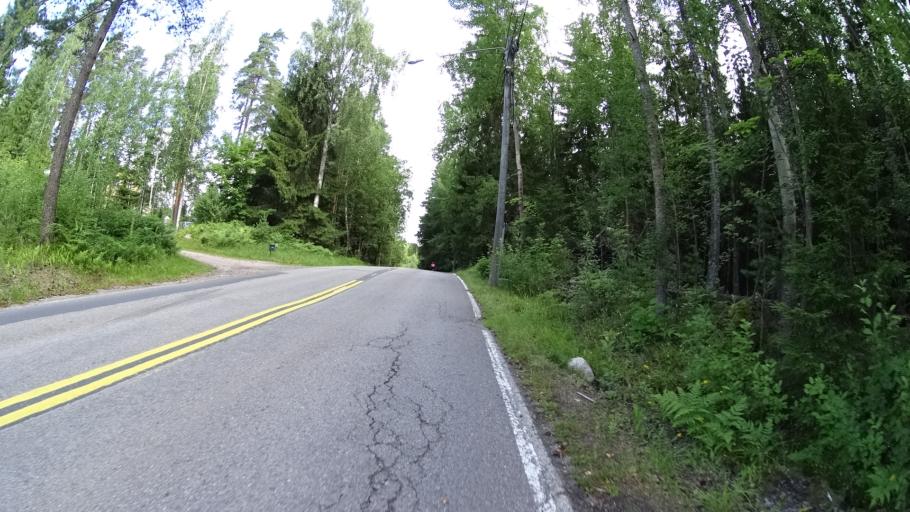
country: FI
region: Uusimaa
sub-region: Helsinki
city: Espoo
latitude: 60.2529
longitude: 24.6532
